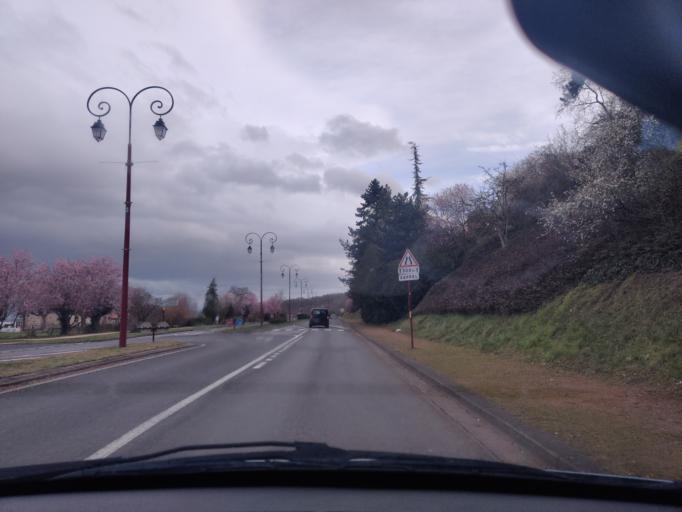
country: FR
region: Auvergne
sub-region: Departement du Puy-de-Dome
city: Chatel-Guyon
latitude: 45.9183
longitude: 3.0745
